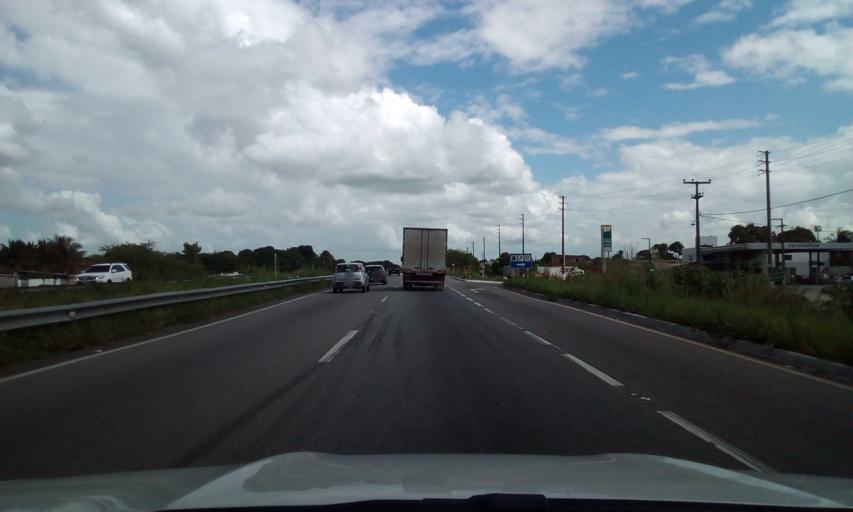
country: BR
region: Paraiba
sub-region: Bayeux
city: Bayeux
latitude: -7.1279
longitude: -34.9518
